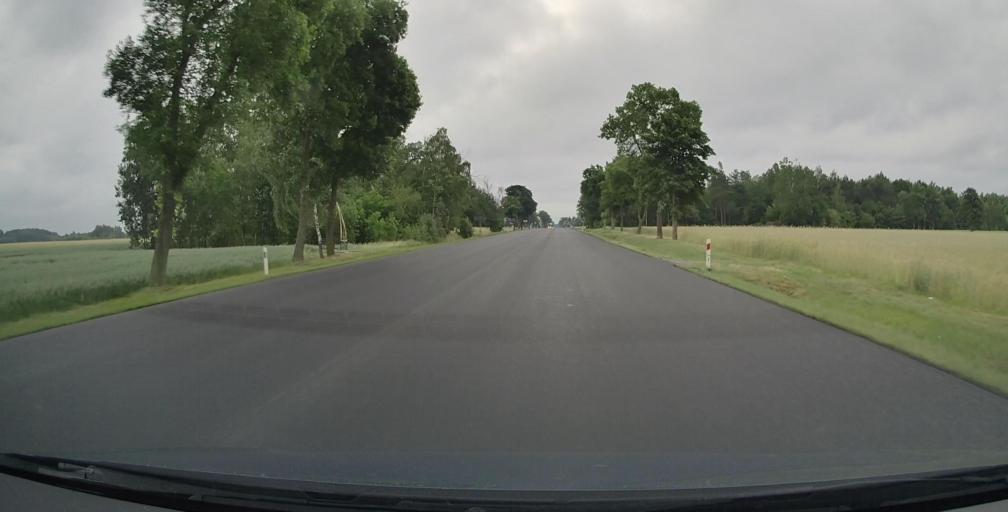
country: PL
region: Lublin Voivodeship
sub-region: Powiat lukowski
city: Trzebieszow
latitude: 52.0547
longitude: 22.6434
